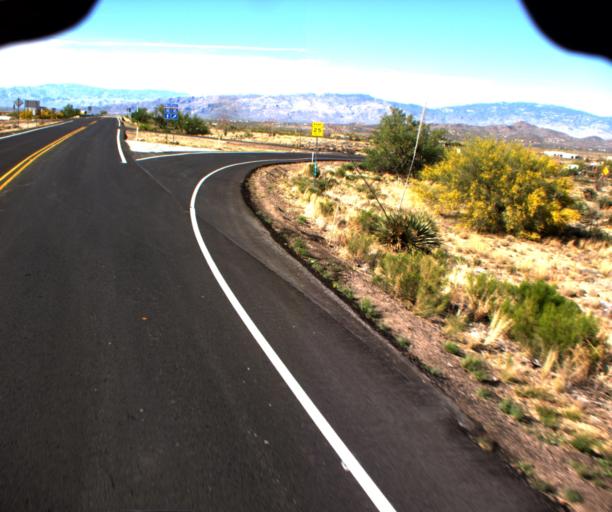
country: US
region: Arizona
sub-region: Pima County
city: Vail
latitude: 32.0044
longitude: -110.6898
